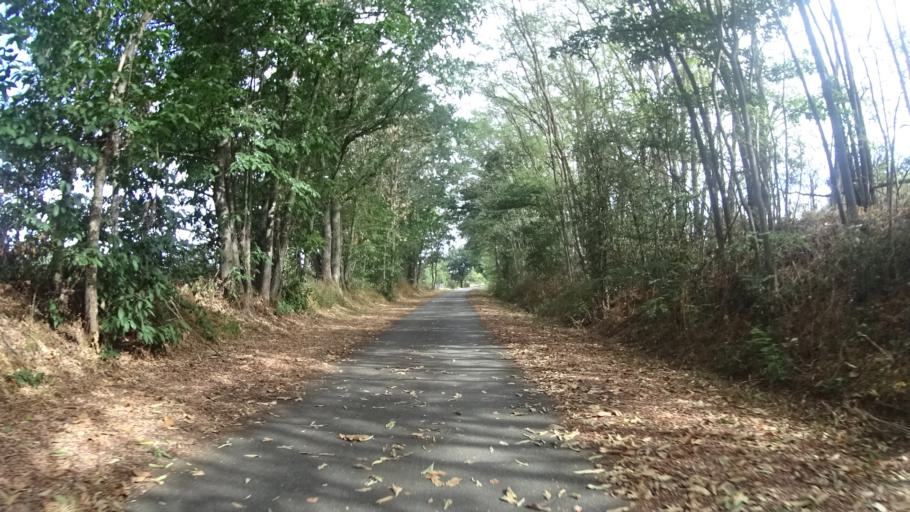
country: FR
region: Auvergne
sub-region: Departement de l'Allier
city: Diou
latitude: 46.5782
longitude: 3.7452
